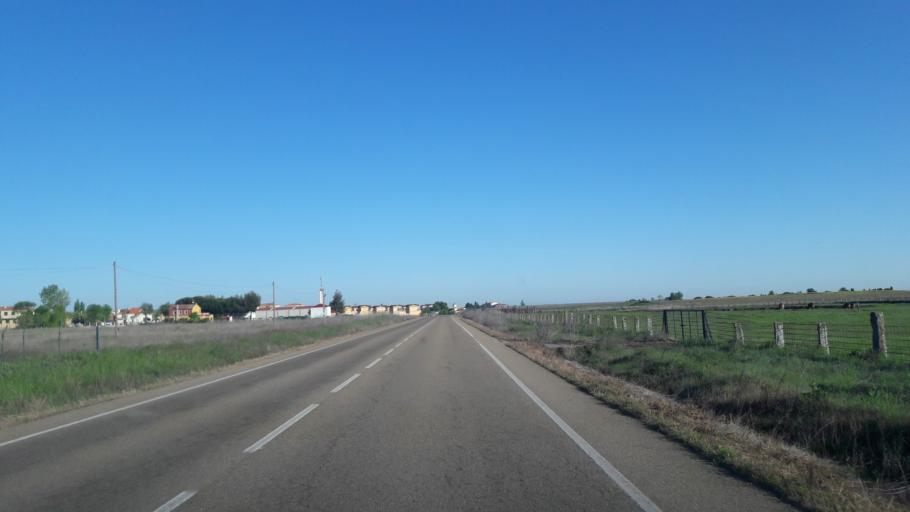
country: ES
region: Castille and Leon
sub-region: Provincia de Salamanca
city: La Fuente de San Esteban
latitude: 40.7962
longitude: -6.2489
